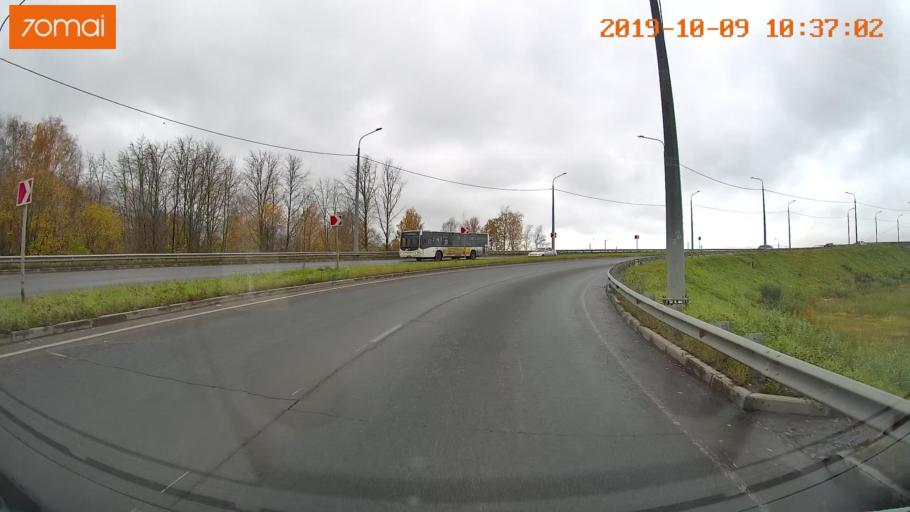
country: RU
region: Vologda
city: Vologda
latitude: 59.2341
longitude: 39.8691
